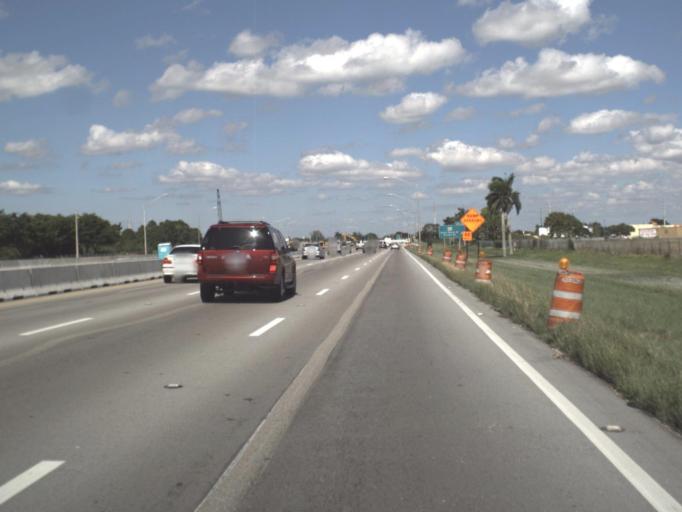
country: US
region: Florida
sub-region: Miami-Dade County
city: South Miami Heights
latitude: 25.5884
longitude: -80.3682
